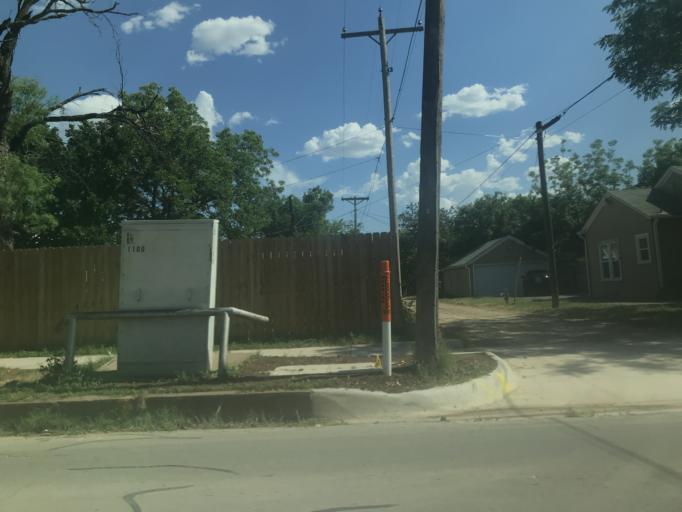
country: US
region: Texas
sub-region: Taylor County
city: Abilene
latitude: 32.4374
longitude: -99.7517
